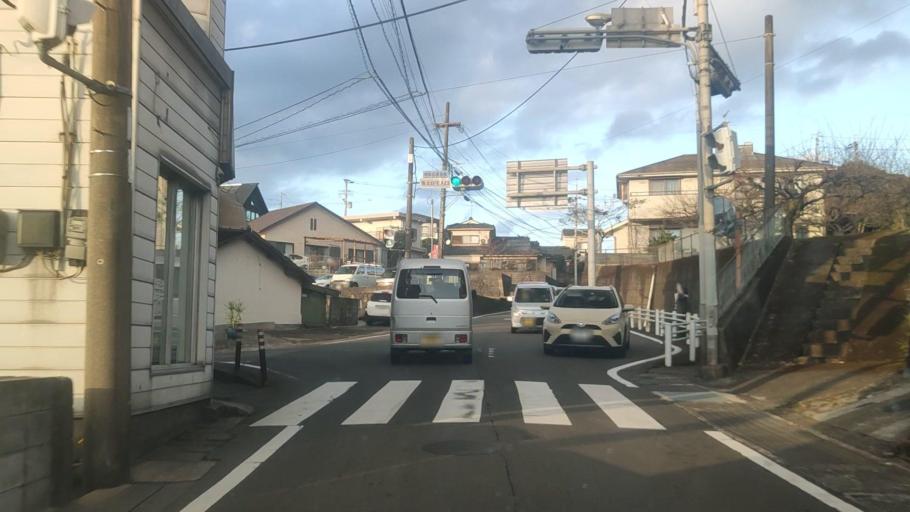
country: JP
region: Kagoshima
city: Kagoshima-shi
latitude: 31.6244
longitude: 130.5527
